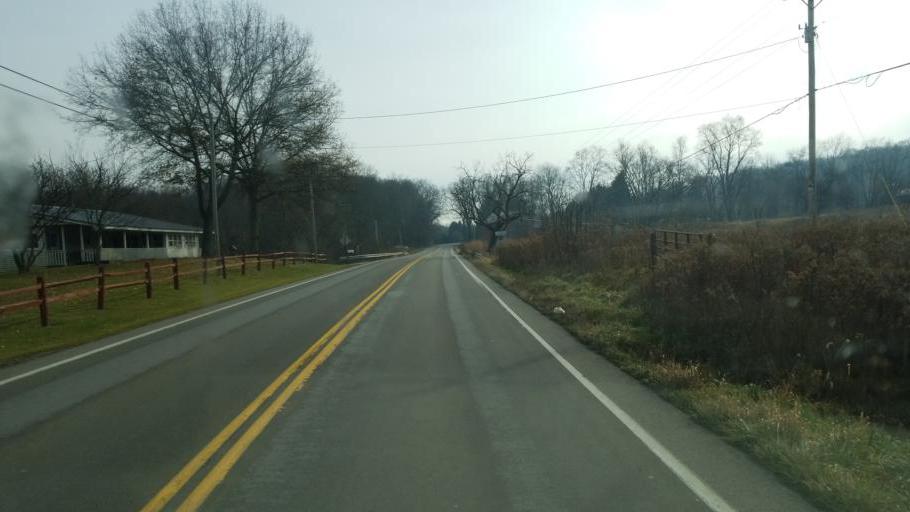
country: US
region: Pennsylvania
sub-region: Crawford County
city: Meadville
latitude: 41.5324
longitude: -80.1619
